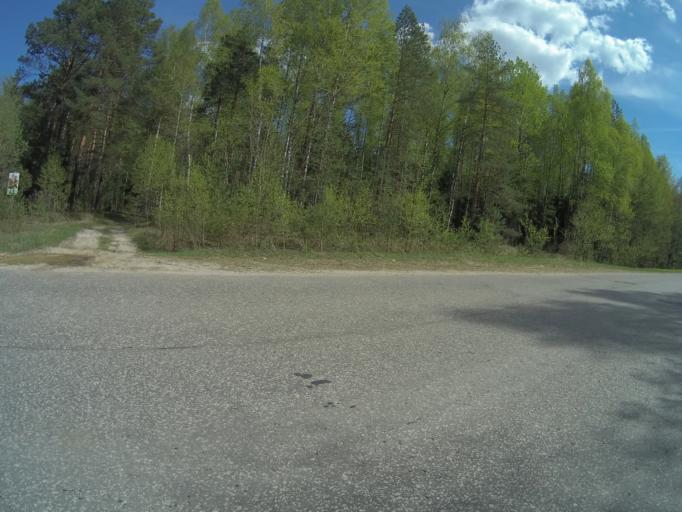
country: RU
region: Vladimir
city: Raduzhnyy
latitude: 55.9786
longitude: 40.2461
